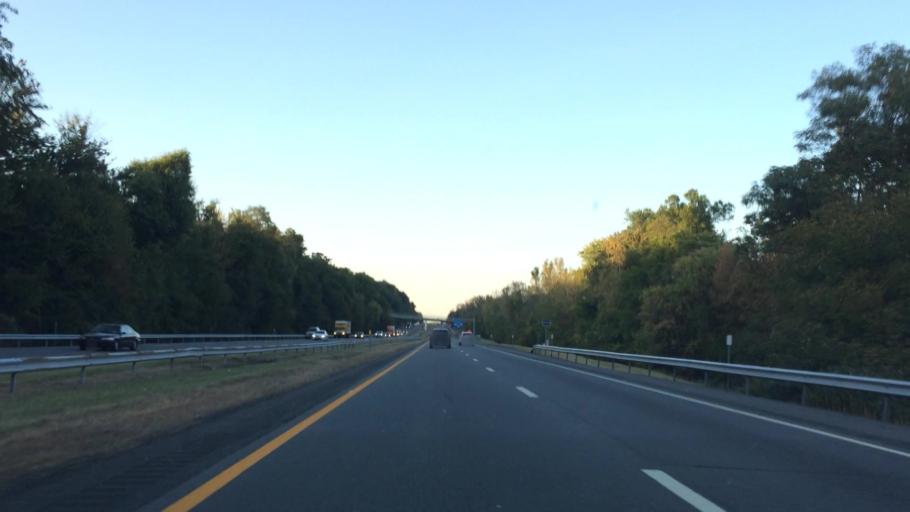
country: US
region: New York
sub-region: Orange County
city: Firthcliffe
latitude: 41.4245
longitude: -74.0685
